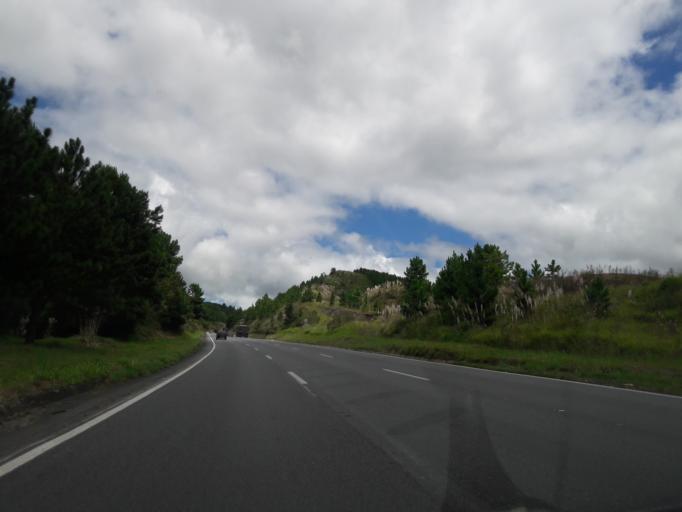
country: BR
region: Parana
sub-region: Campina Grande Do Sul
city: Campina Grande do Sul
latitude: -25.1022
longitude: -48.8329
